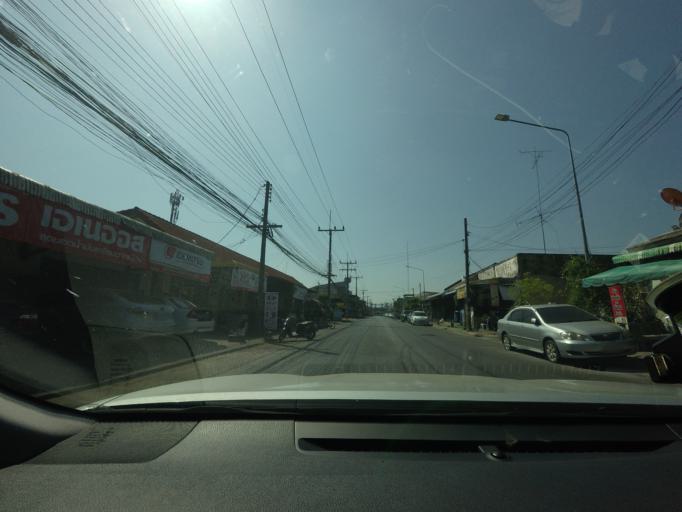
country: TH
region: Yala
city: Yala
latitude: 6.5432
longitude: 101.2876
